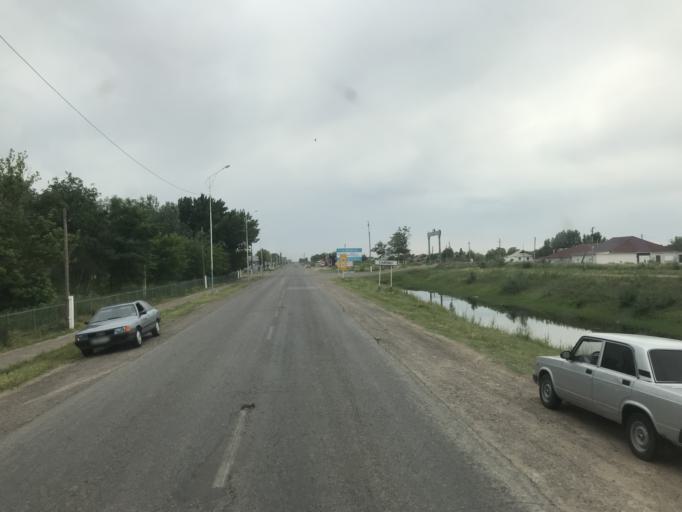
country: KZ
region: Ongtustik Qazaqstan
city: Asykata
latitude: 40.9354
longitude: 68.4103
